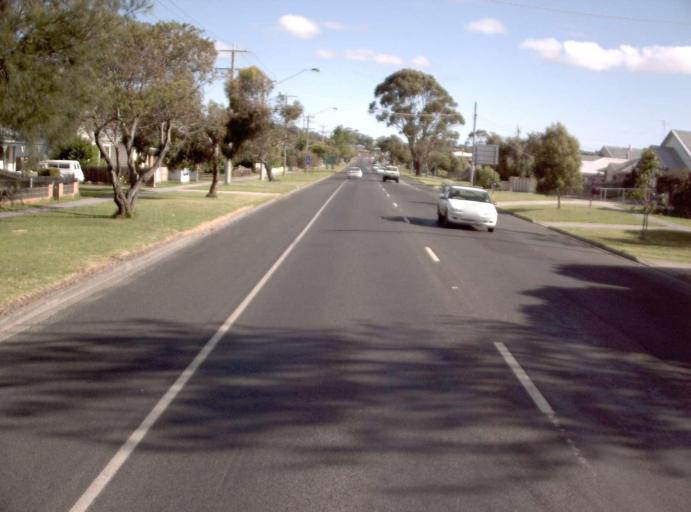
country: AU
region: Victoria
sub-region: Bass Coast
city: North Wonthaggi
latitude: -38.5992
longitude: 145.5926
